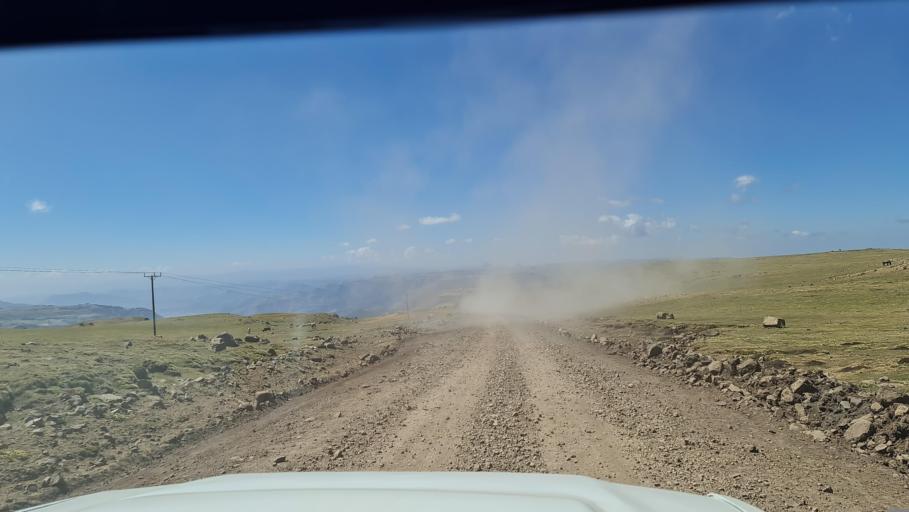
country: ET
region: Amhara
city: Debark'
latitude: 13.2386
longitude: 38.1150
